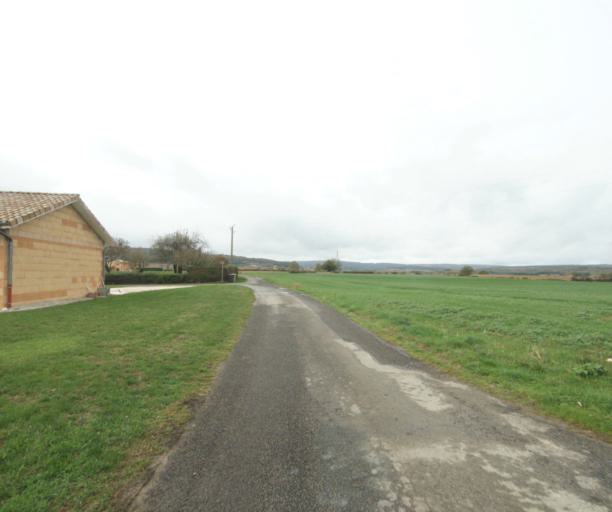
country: FR
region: Rhone-Alpes
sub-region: Departement de l'Ain
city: Pont-de-Vaux
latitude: 46.4668
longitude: 4.8789
